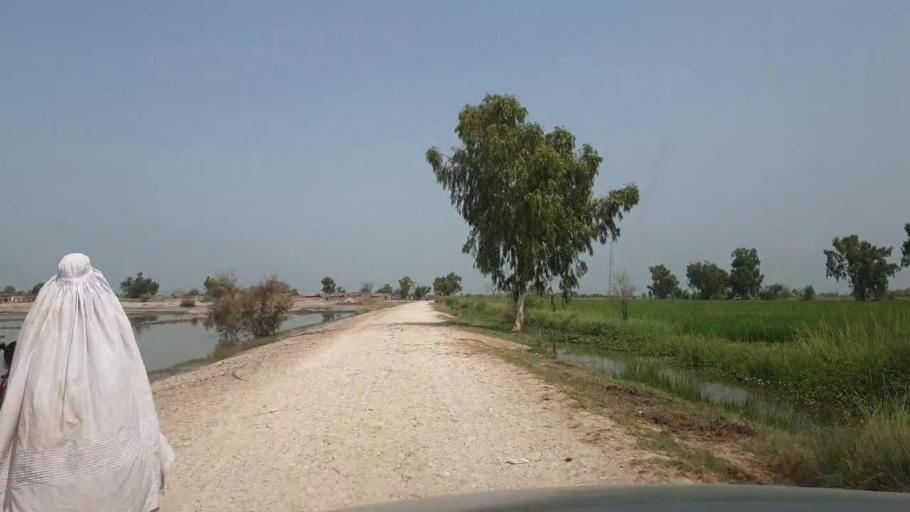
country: PK
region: Sindh
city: Madeji
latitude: 27.7981
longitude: 68.5325
